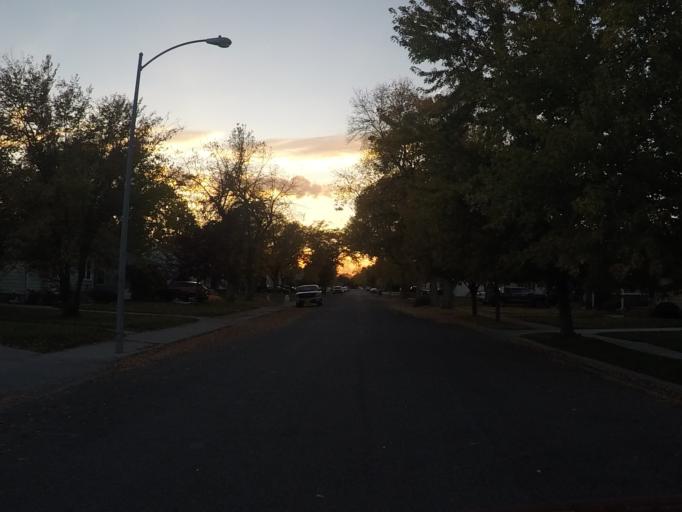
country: US
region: Montana
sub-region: Yellowstone County
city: Billings
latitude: 45.7869
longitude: -108.5447
